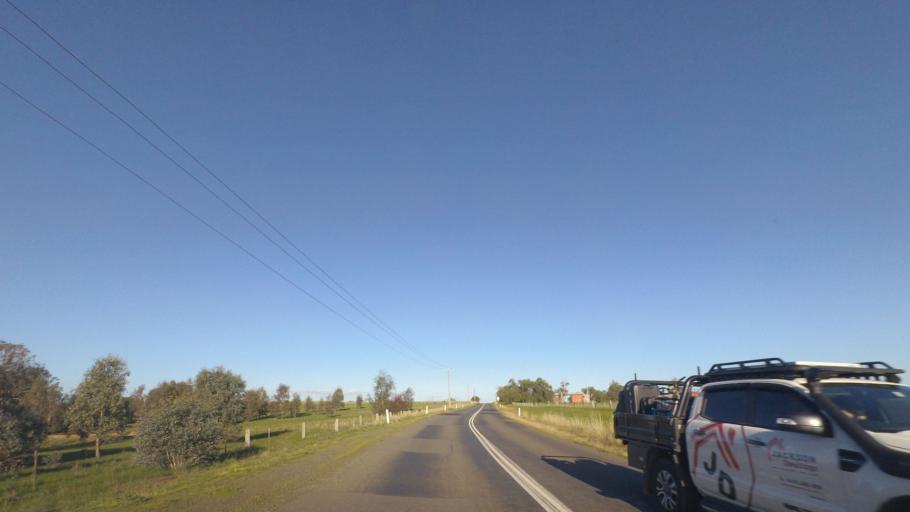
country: AU
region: Victoria
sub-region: Greater Bendigo
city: Kennington
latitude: -36.8158
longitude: 144.5127
